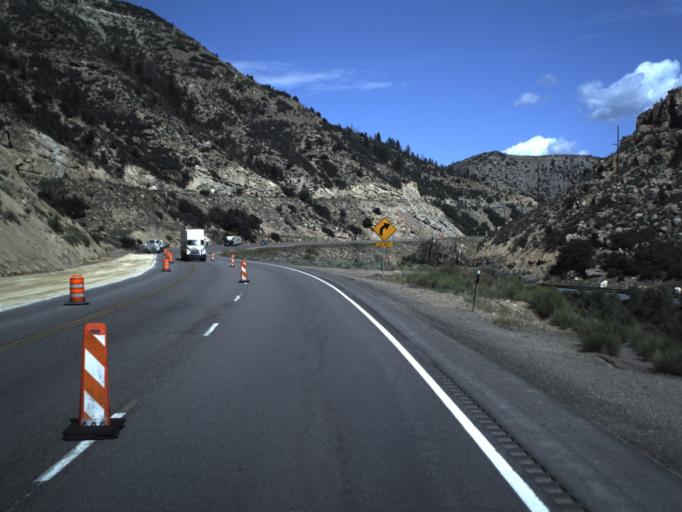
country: US
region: Utah
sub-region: Carbon County
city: Helper
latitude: 39.7886
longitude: -110.9292
